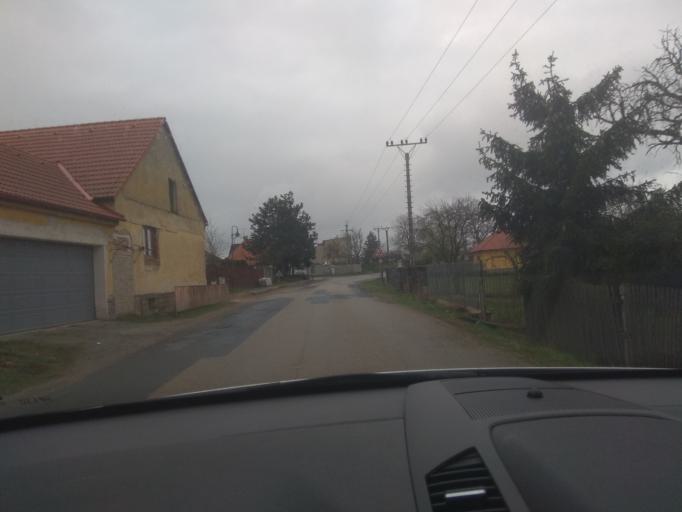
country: CZ
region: South Moravian
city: Zastavka
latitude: 49.1718
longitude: 16.3599
